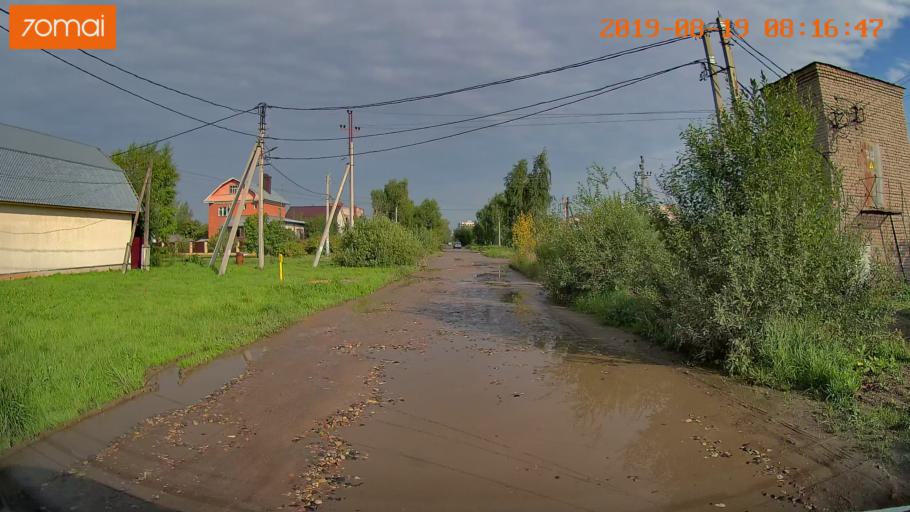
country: RU
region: Ivanovo
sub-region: Gorod Ivanovo
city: Ivanovo
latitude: 56.9752
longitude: 40.9984
